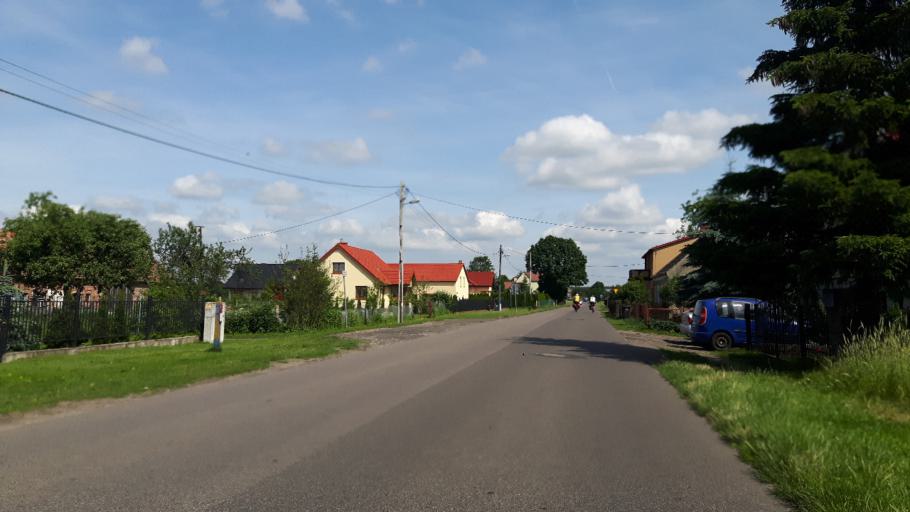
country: PL
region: West Pomeranian Voivodeship
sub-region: Powiat goleniowski
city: Goleniow
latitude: 53.4935
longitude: 14.7771
